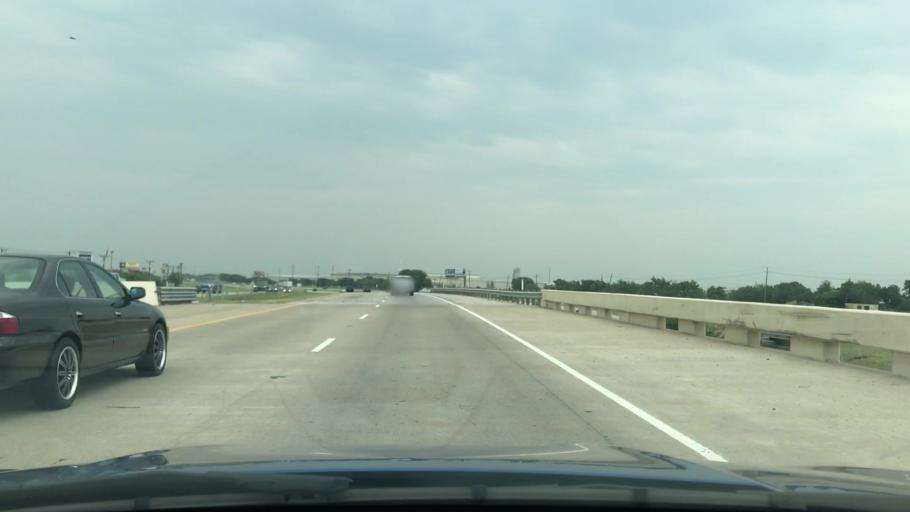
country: US
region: Texas
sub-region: Kaufman County
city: Forney
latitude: 32.7426
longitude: -96.4487
